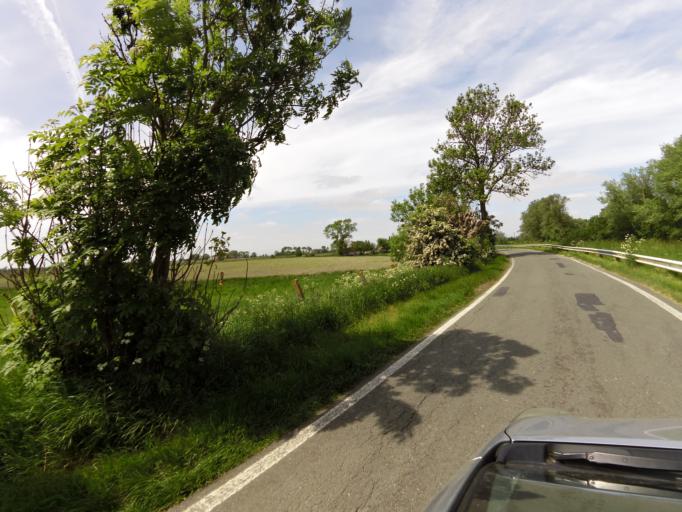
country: BE
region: Flanders
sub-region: Provincie West-Vlaanderen
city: Diksmuide
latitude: 51.0179
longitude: 2.8497
